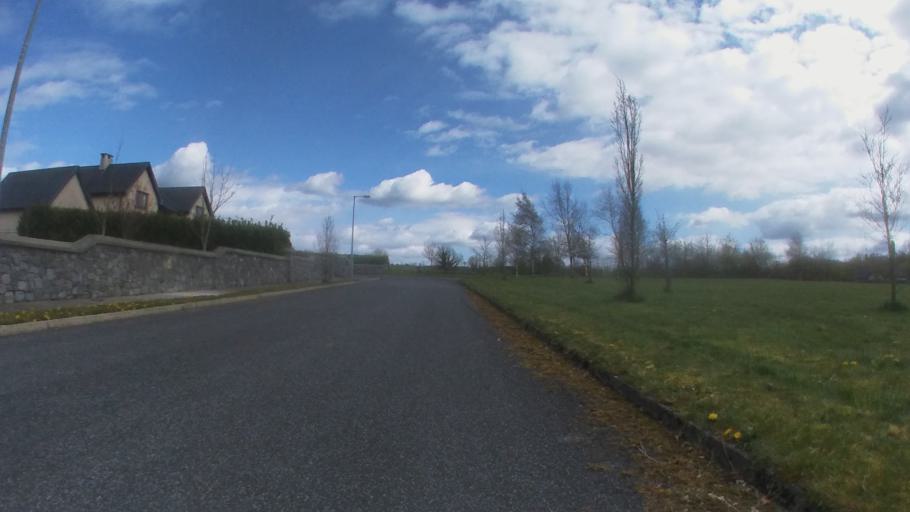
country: IE
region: Leinster
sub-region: Kilkenny
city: Kilkenny
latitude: 52.7187
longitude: -7.2325
